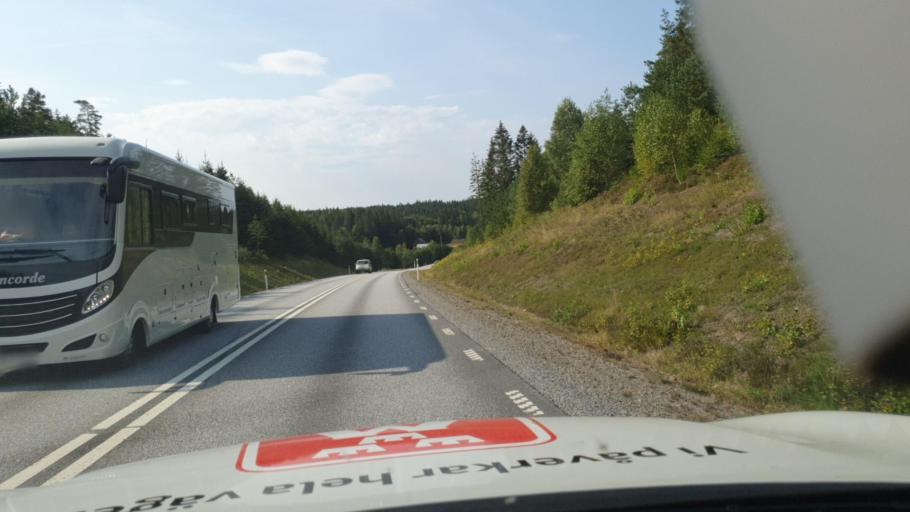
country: SE
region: Vaestra Goetaland
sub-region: Tanums Kommun
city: Tanumshede
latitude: 58.8017
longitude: 11.5959
